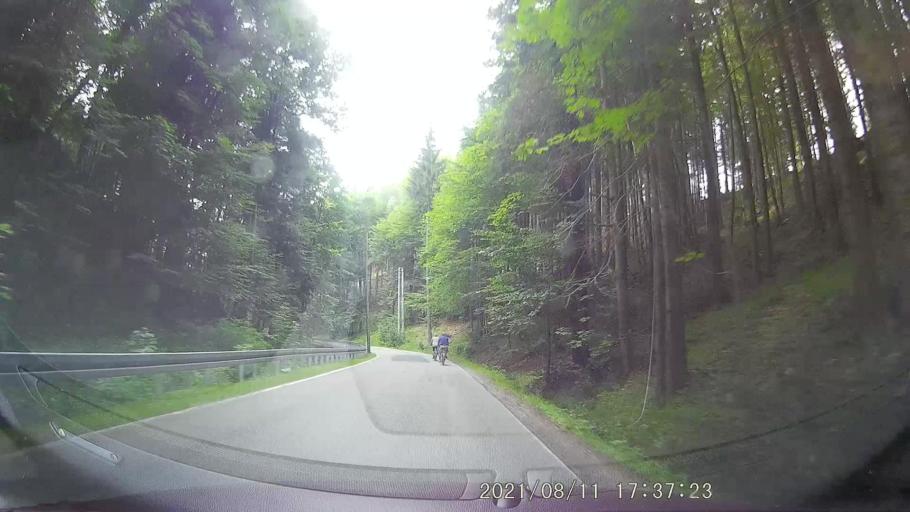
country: PL
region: Lower Silesian Voivodeship
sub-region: Powiat klodzki
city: Duszniki-Zdroj
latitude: 50.3378
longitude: 16.4047
